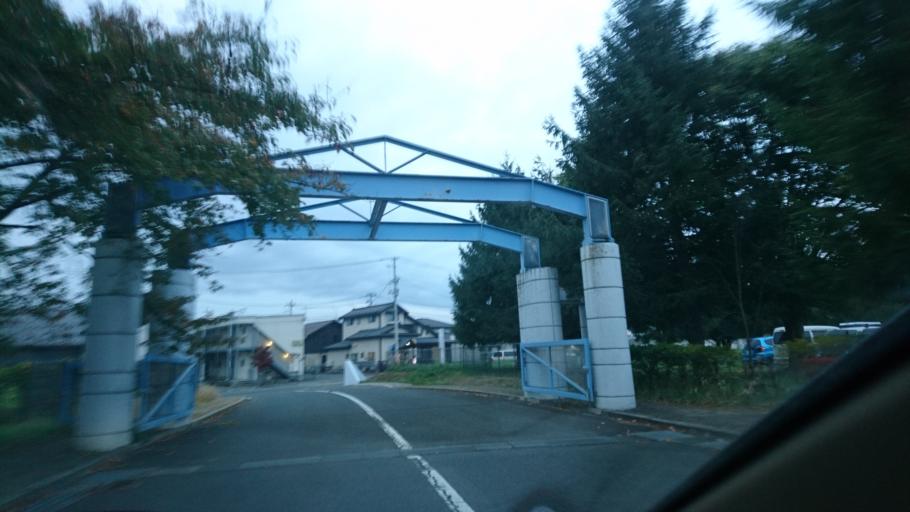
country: JP
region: Iwate
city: Morioka-shi
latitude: 39.6754
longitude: 141.1316
